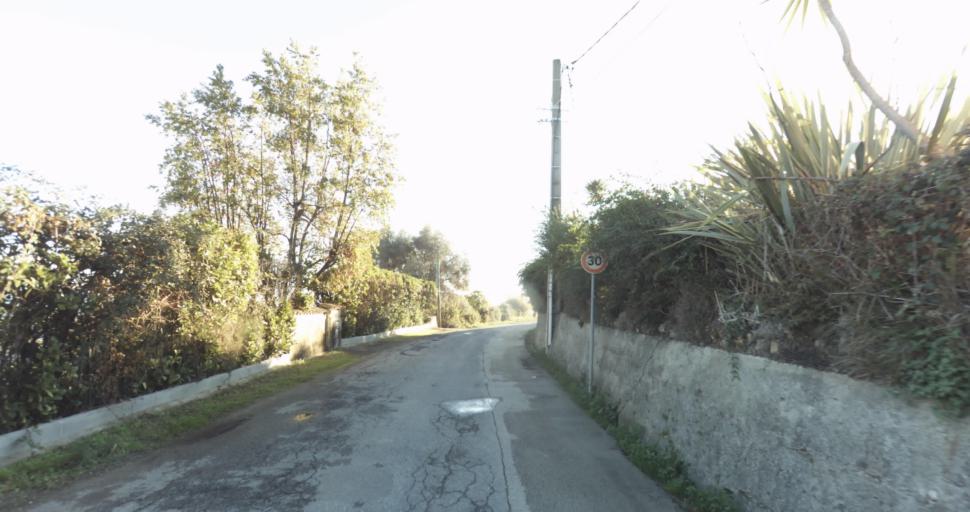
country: FR
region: Provence-Alpes-Cote d'Azur
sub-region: Departement des Alpes-Maritimes
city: Vence
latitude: 43.7354
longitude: 7.1213
